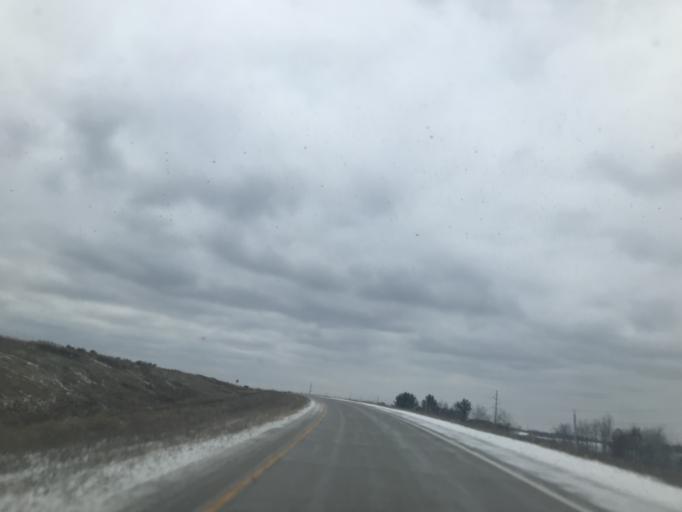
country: US
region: Wisconsin
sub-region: Marinette County
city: Peshtigo
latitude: 45.0588
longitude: -87.7160
